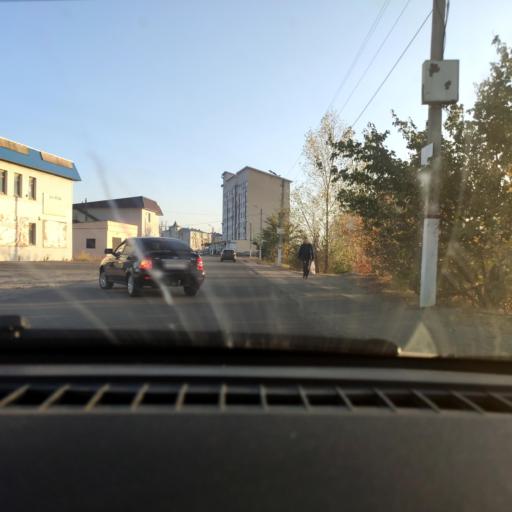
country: RU
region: Voronezj
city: Novaya Usman'
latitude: 51.6094
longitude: 39.3876
